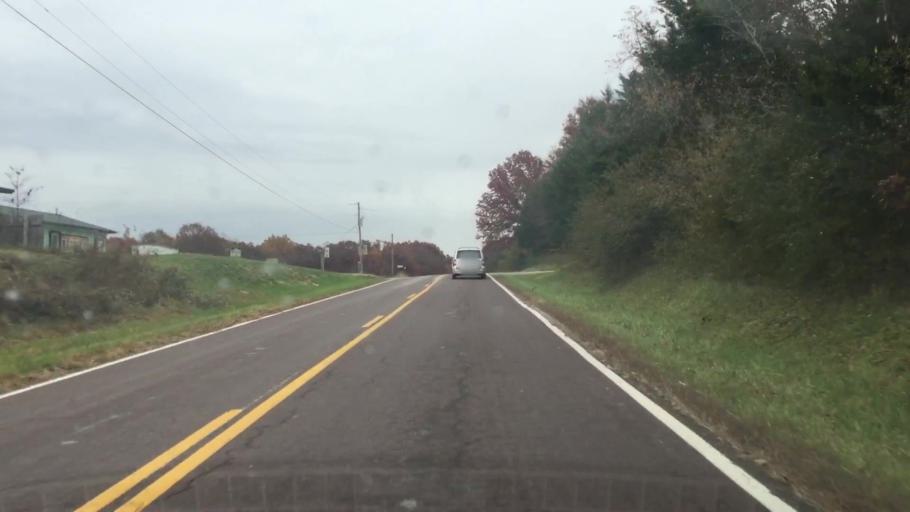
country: US
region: Missouri
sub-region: Callaway County
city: Fulton
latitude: 38.7870
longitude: -91.7649
